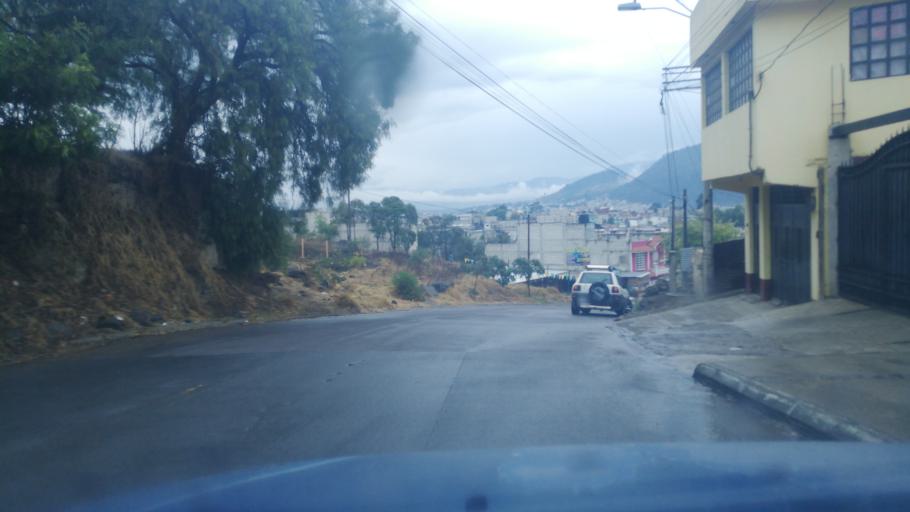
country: GT
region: Quetzaltenango
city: Quetzaltenango
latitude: 14.8333
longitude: -91.5322
